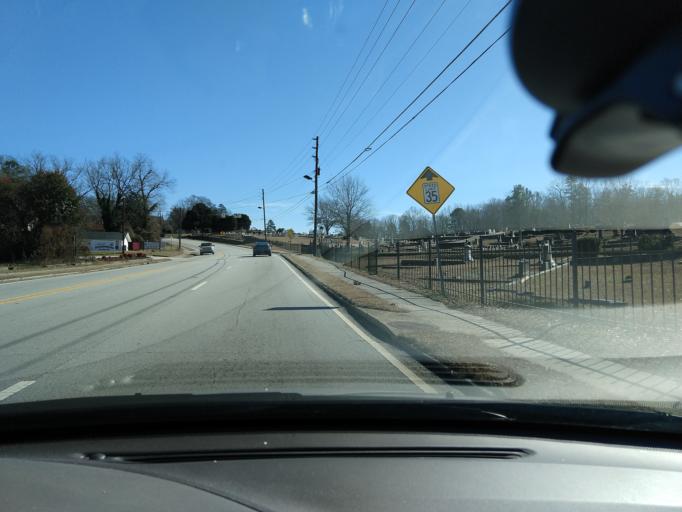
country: US
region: Georgia
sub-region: Stephens County
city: Toccoa
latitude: 34.5851
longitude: -83.3369
